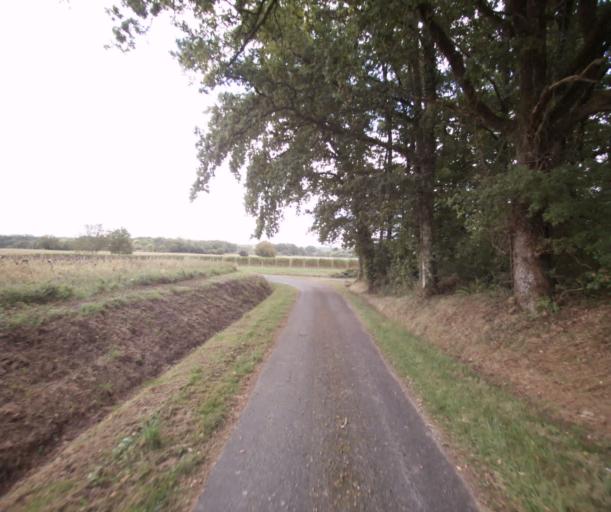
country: FR
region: Midi-Pyrenees
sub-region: Departement du Gers
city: Cazaubon
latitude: 43.9131
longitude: -0.0697
